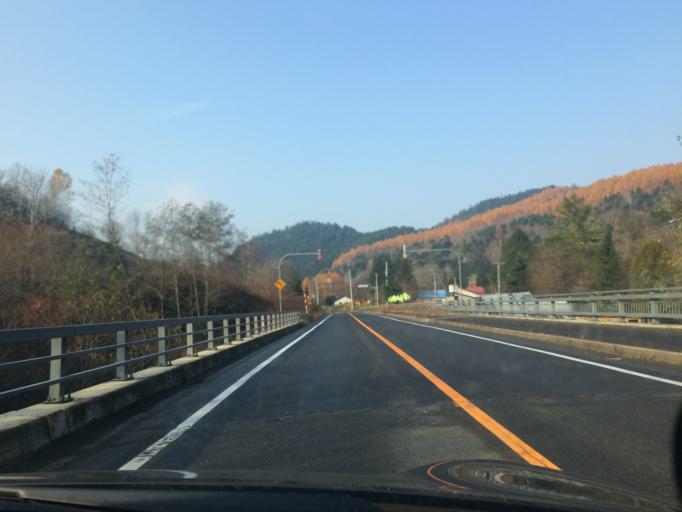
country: JP
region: Hokkaido
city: Iwamizawa
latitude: 42.9341
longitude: 142.0796
